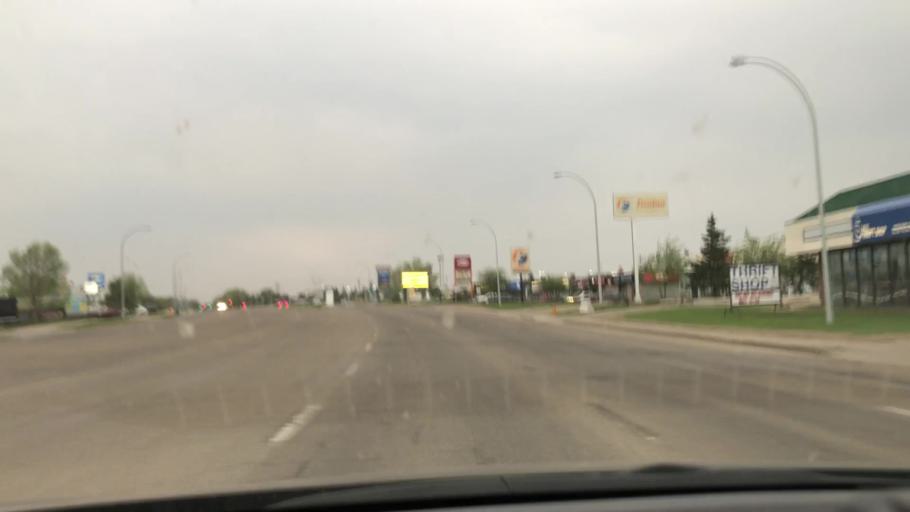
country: CA
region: Alberta
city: Edmonton
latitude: 53.4655
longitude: -113.4736
